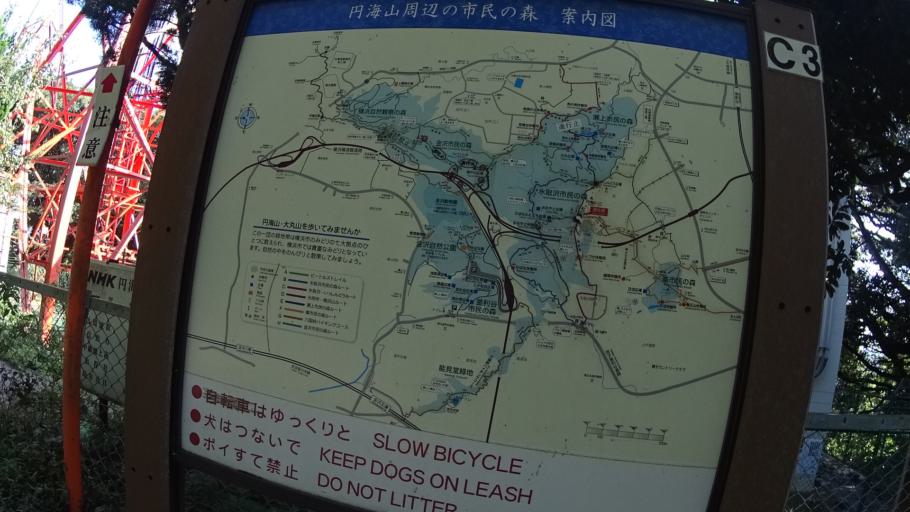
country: JP
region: Kanagawa
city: Kamakura
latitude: 35.3603
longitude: 139.5958
